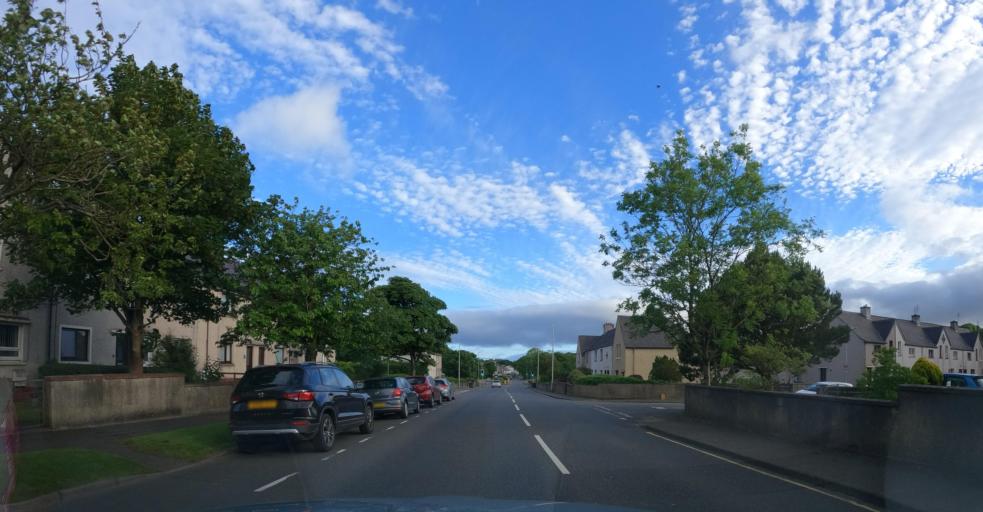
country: GB
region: Scotland
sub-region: Eilean Siar
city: Isle of Lewis
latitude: 58.2184
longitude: -6.3859
